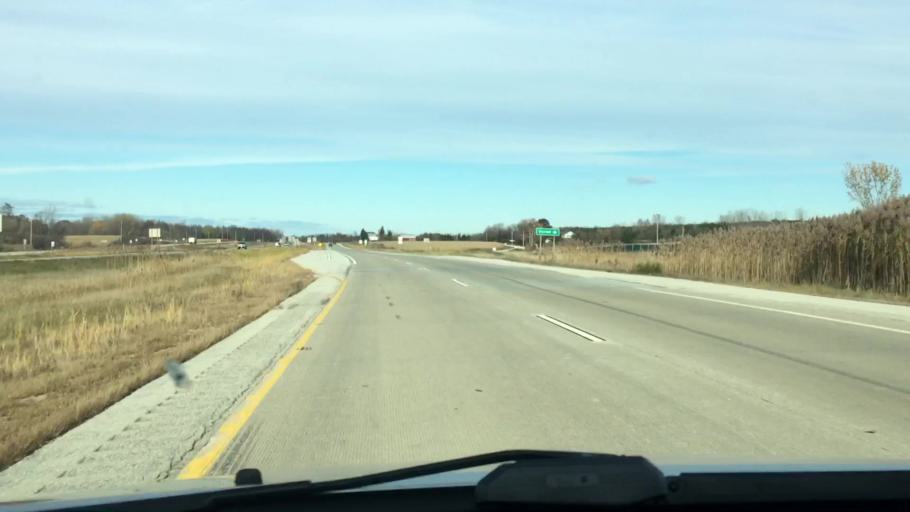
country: US
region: Wisconsin
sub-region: Kewaunee County
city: Luxemburg
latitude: 44.6571
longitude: -87.7476
